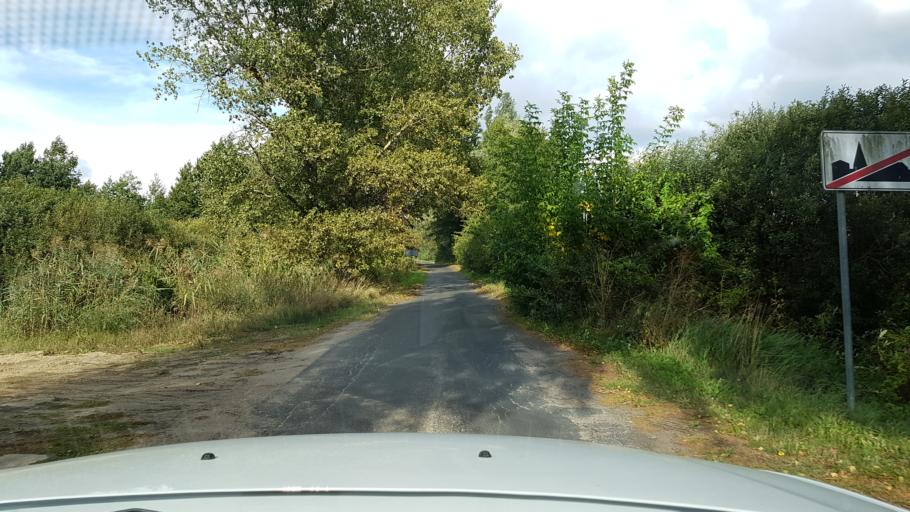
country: PL
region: West Pomeranian Voivodeship
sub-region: Powiat gryfinski
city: Gryfino
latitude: 53.2971
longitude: 14.5046
